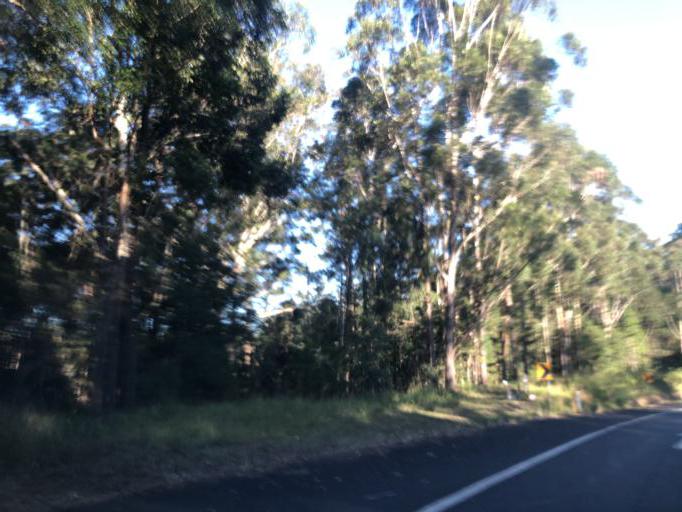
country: AU
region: New South Wales
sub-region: Nambucca Shire
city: Nambucca
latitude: -30.5503
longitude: 153.0087
